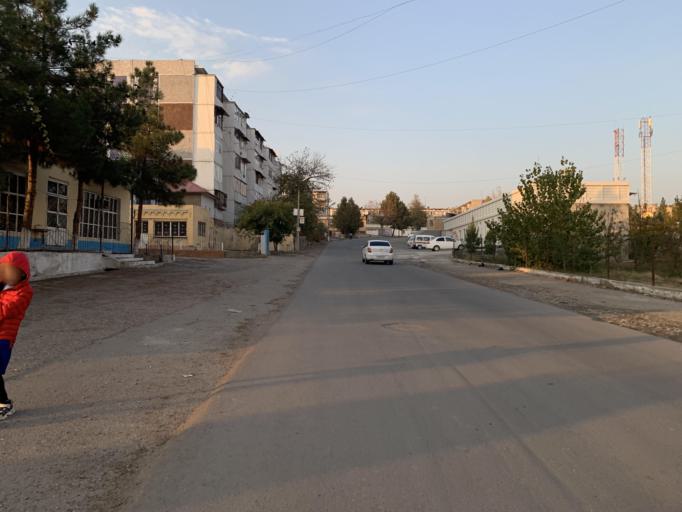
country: UZ
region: Namangan
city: Namangan Shahri
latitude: 41.0035
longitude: 71.5989
